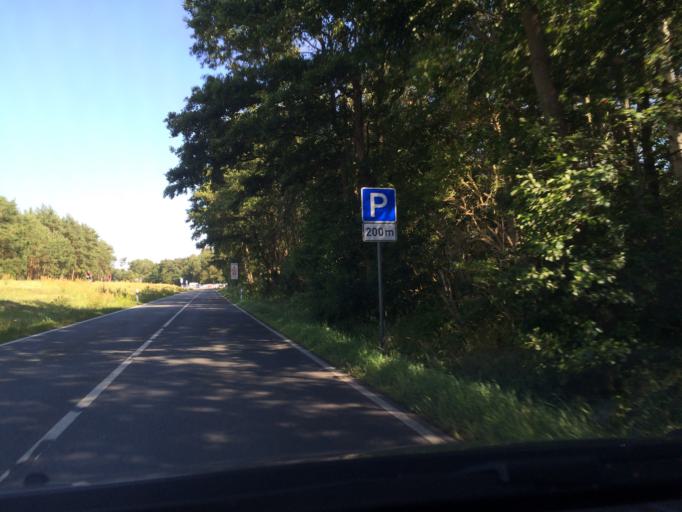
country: DE
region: Mecklenburg-Vorpommern
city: Ostseebad Prerow
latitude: 54.4490
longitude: 12.6024
